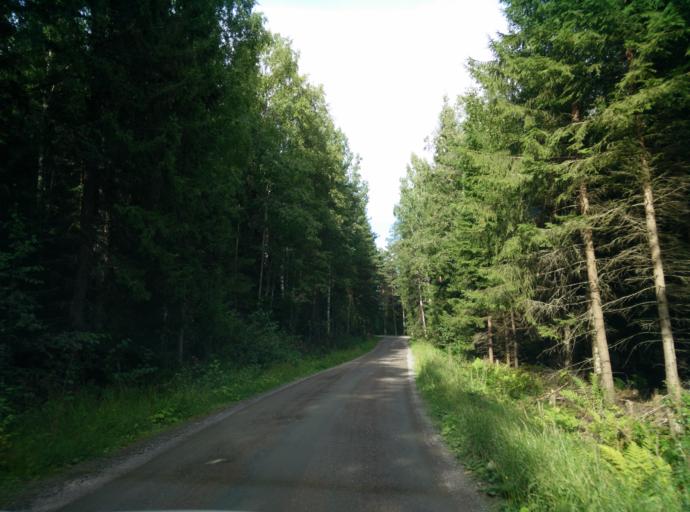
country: FI
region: Haeme
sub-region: Haemeenlinna
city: Kalvola
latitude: 61.1281
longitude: 24.1414
